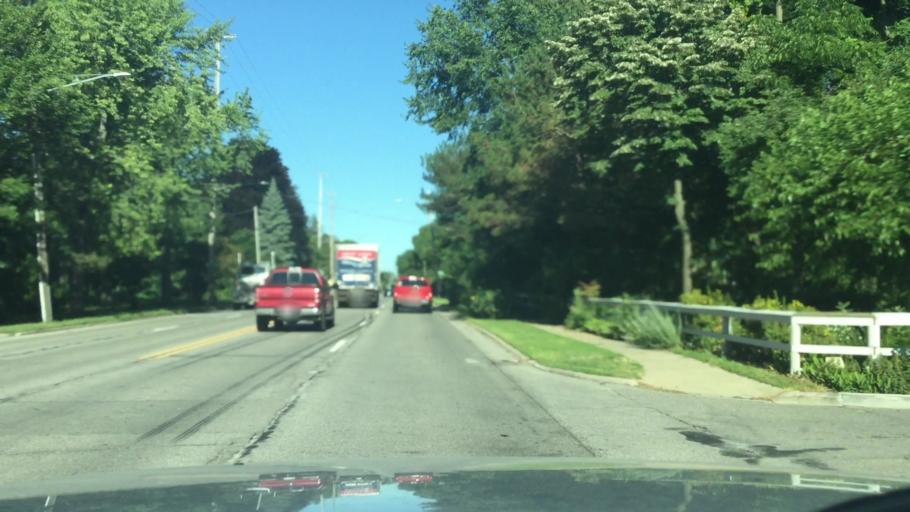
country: US
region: Michigan
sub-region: Saginaw County
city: Saginaw
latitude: 43.4152
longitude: -83.9930
